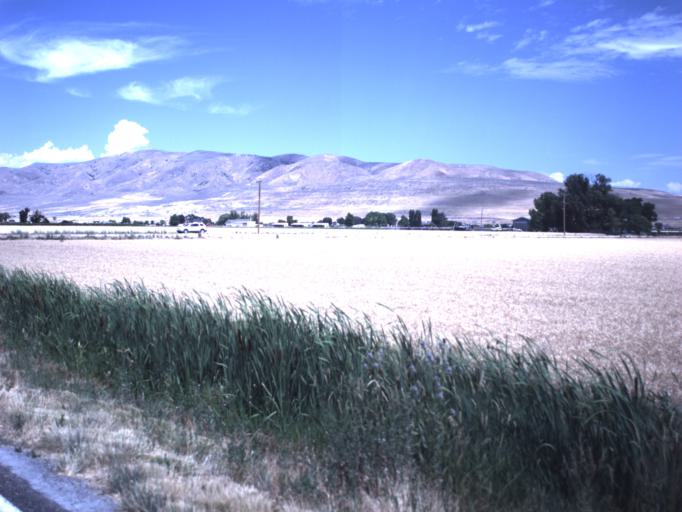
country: US
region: Utah
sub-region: Box Elder County
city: Tremonton
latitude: 41.7082
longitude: -112.2781
